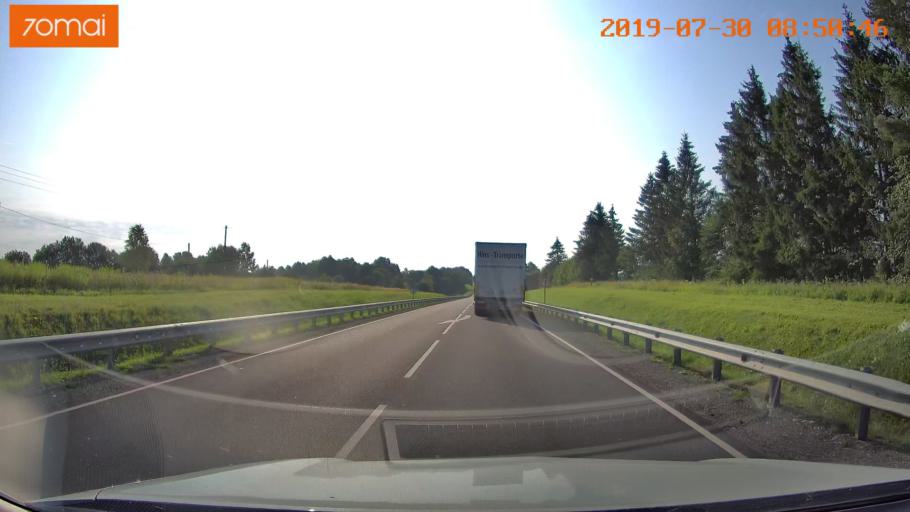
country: RU
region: Kaliningrad
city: Chernyakhovsk
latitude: 54.6055
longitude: 21.9450
